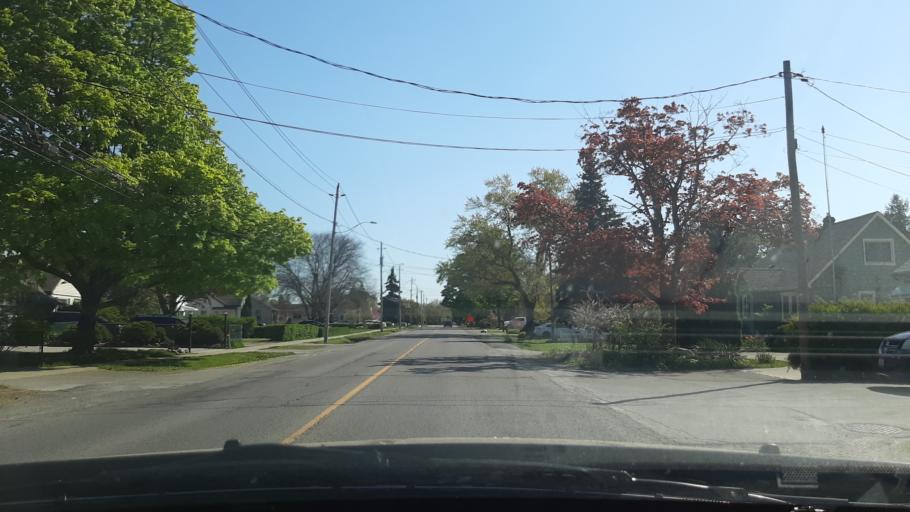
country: CA
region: Ontario
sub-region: Regional Municipality of Niagara
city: St. Catharines
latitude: 43.1982
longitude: -79.2241
